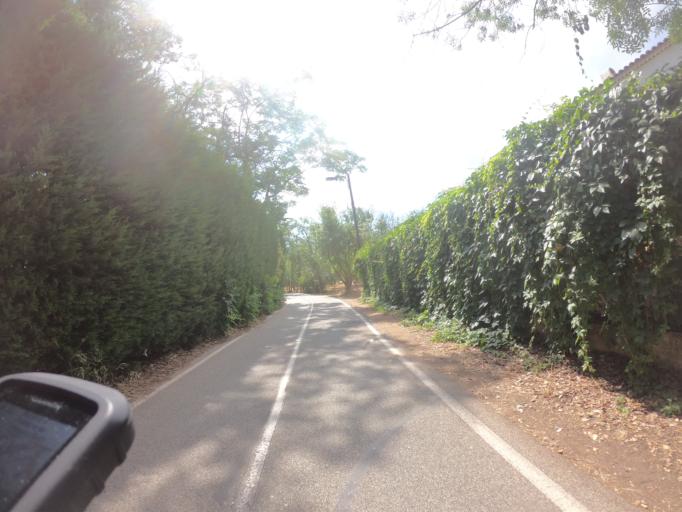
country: FR
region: Provence-Alpes-Cote d'Azur
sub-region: Departement du Var
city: La Valette-du-Var
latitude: 43.1169
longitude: 5.9731
